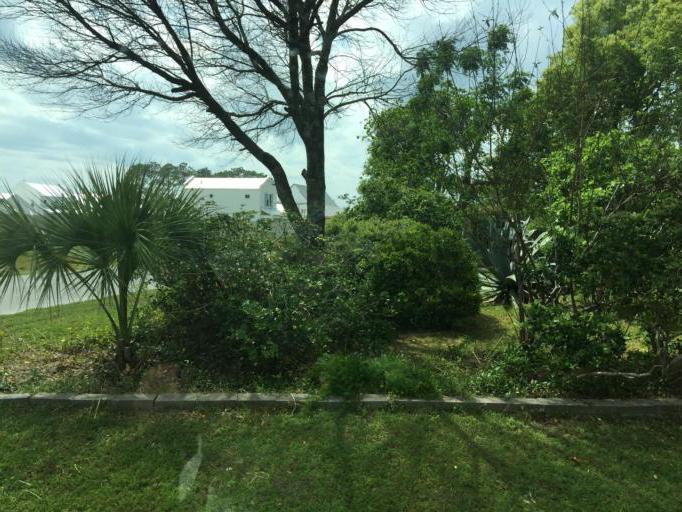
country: US
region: Florida
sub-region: Bay County
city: Laguna Beach
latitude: 30.2262
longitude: -85.8871
